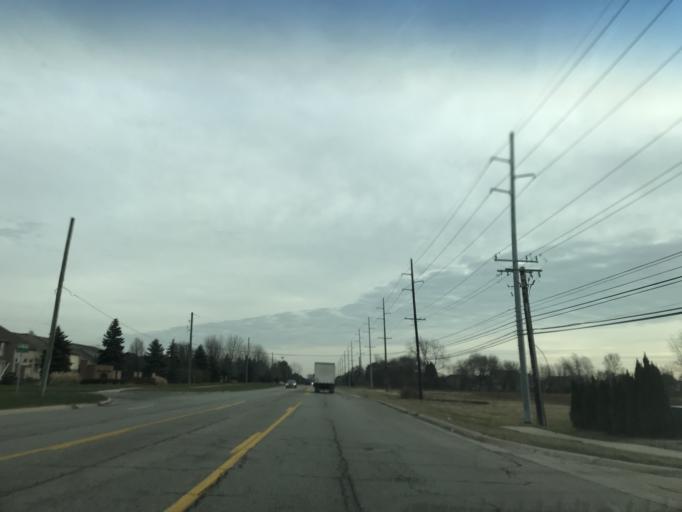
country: US
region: Michigan
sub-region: Macomb County
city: Clinton
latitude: 42.6720
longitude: -82.9380
